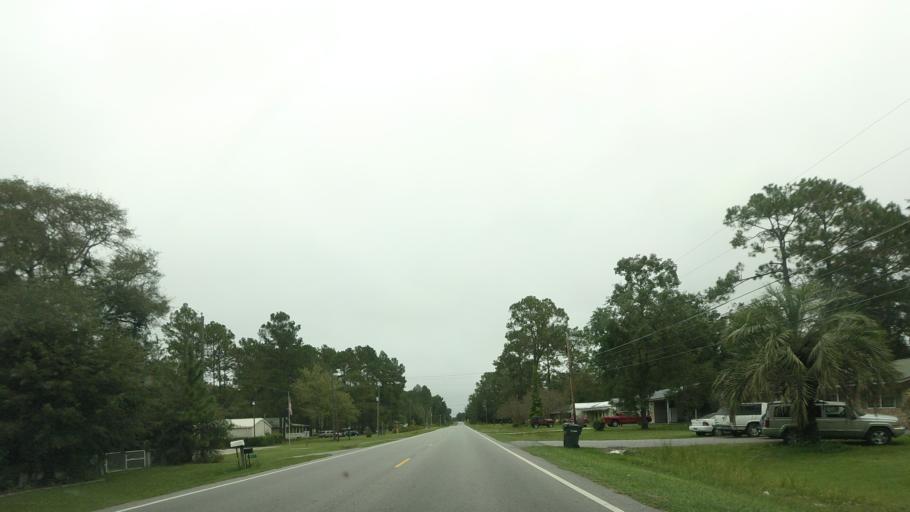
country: US
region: Georgia
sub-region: Berrien County
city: Nashville
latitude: 31.2230
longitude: -83.2481
